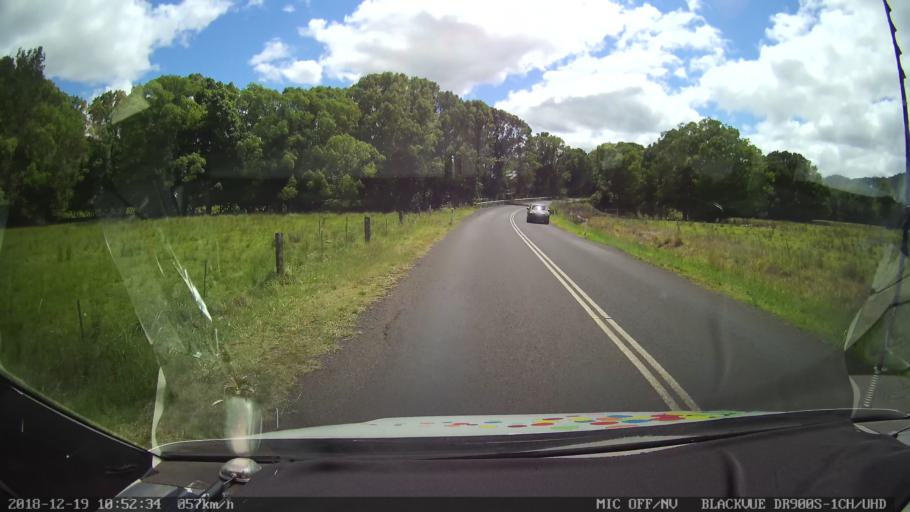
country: AU
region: New South Wales
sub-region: Lismore Municipality
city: Nimbin
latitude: -28.5915
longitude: 153.2310
